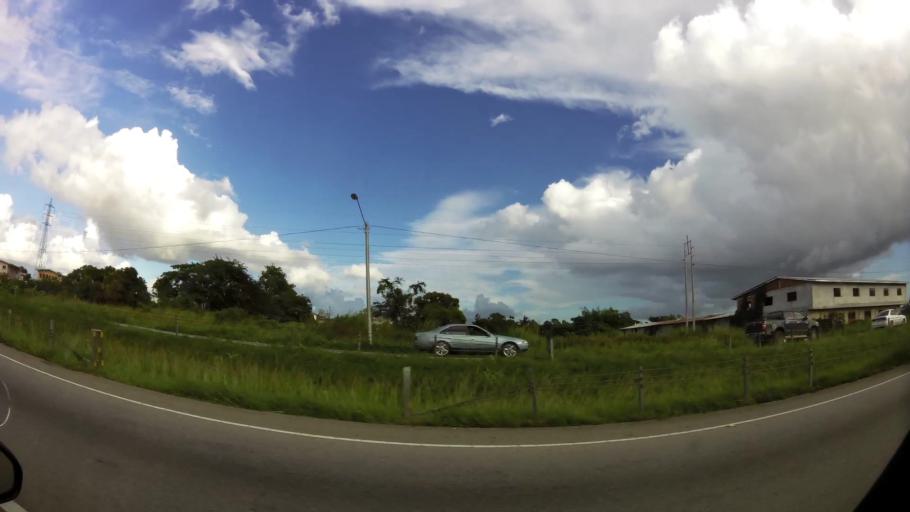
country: TT
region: Chaguanas
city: Chaguanas
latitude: 10.4577
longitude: -61.4106
